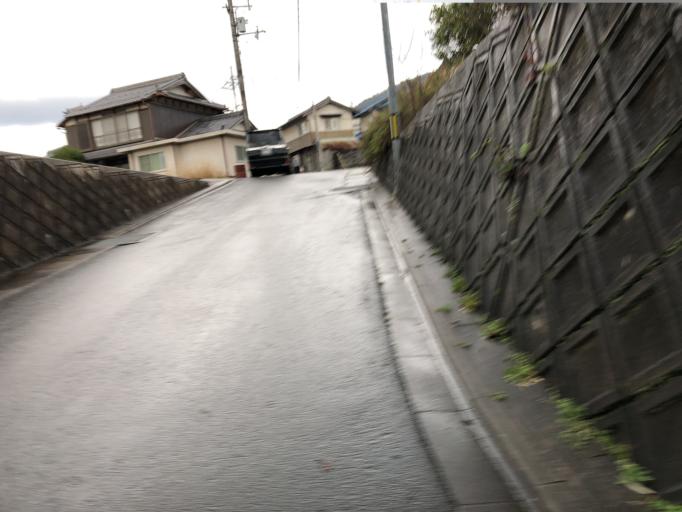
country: JP
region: Kyoto
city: Kameoka
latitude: 35.0219
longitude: 135.5951
